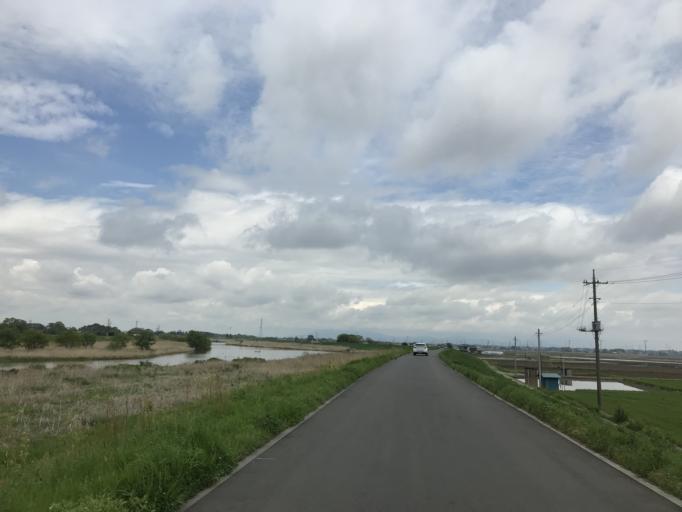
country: JP
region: Ibaraki
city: Mitsukaido
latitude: 35.9930
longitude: 139.9907
